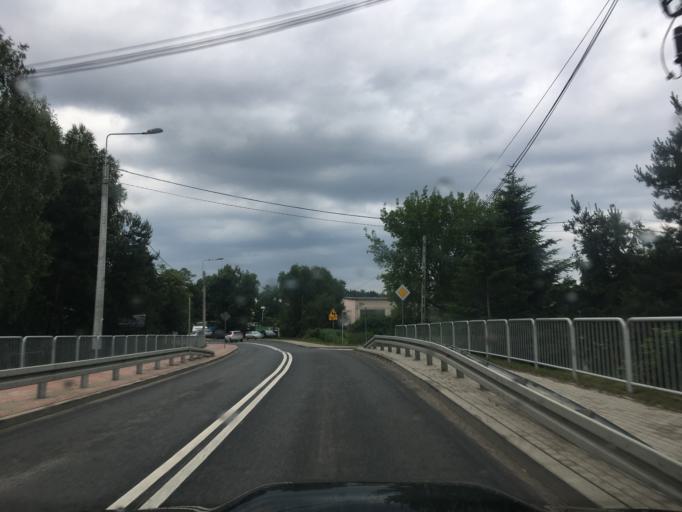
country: PL
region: Masovian Voivodeship
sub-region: Powiat piaseczynski
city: Piaseczno
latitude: 52.0461
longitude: 20.9906
